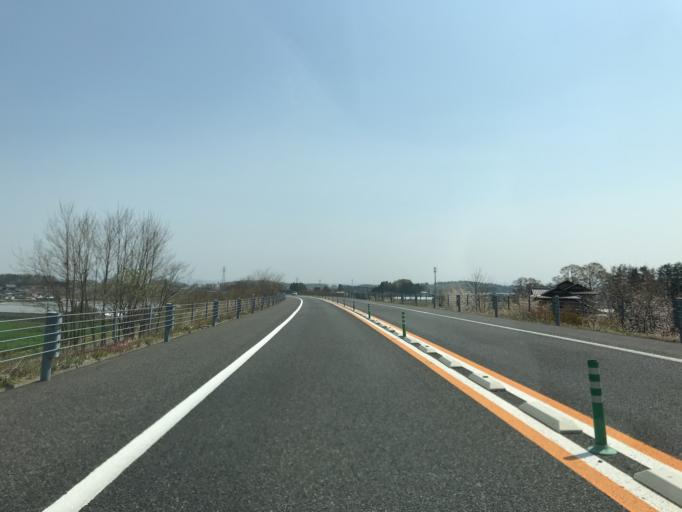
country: JP
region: Fukushima
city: Sukagawa
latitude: 37.1878
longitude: 140.3240
